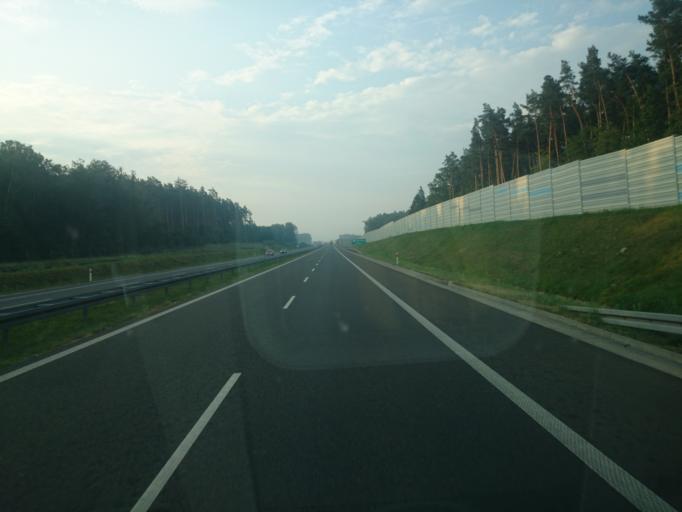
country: PL
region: West Pomeranian Voivodeship
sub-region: Powiat mysliborski
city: Mysliborz
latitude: 52.9720
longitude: 14.9093
